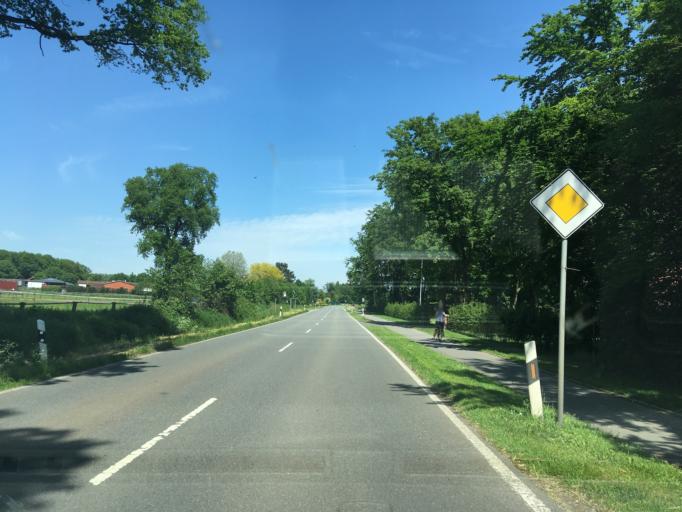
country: DE
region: North Rhine-Westphalia
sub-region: Regierungsbezirk Munster
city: Borken
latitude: 51.8889
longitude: 6.8191
